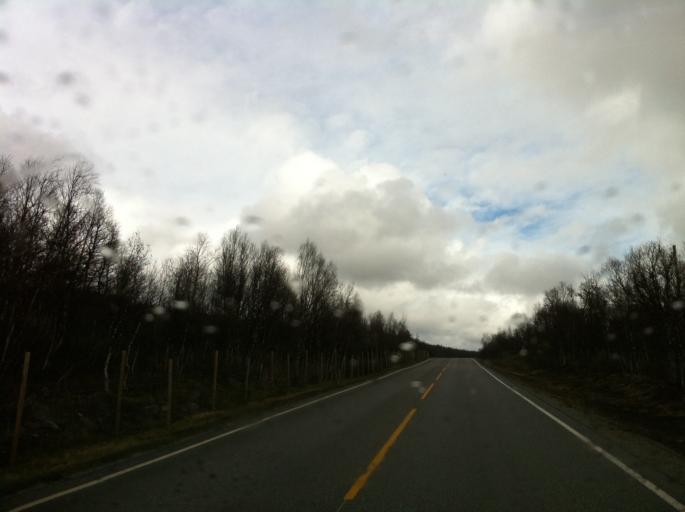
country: NO
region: Sor-Trondelag
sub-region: Tydal
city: Aas
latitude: 62.6392
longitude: 11.9028
